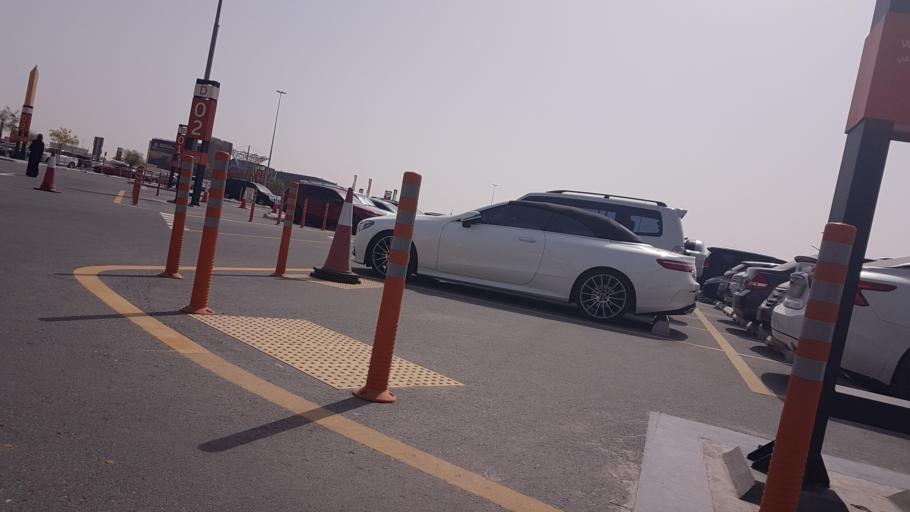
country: AE
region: Dubai
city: Dubai
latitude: 24.9655
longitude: 55.1572
